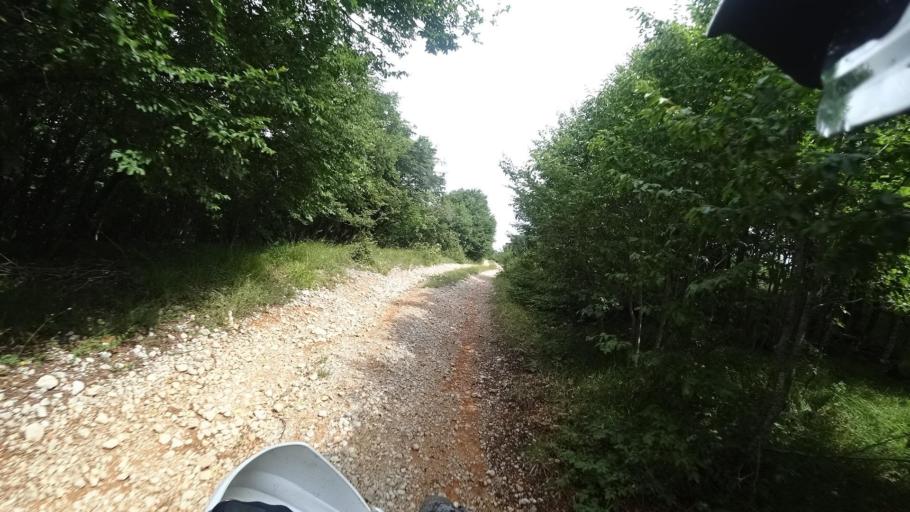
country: BA
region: Federation of Bosnia and Herzegovina
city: Bihac
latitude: 44.6530
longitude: 15.7590
